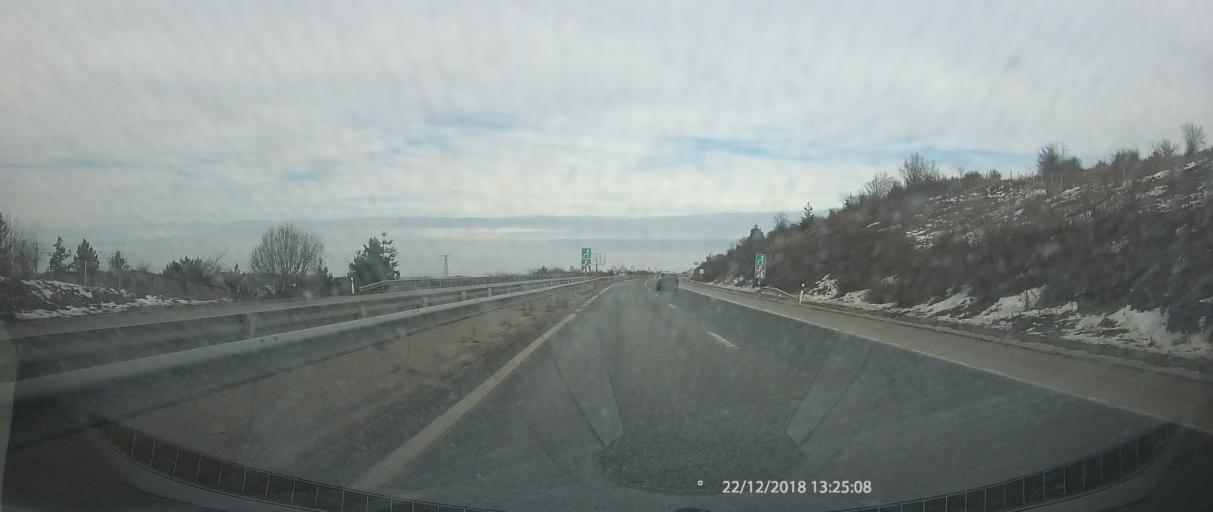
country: BG
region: Lovech
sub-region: Obshtina Yablanitsa
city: Yablanitsa
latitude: 43.0318
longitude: 24.1173
